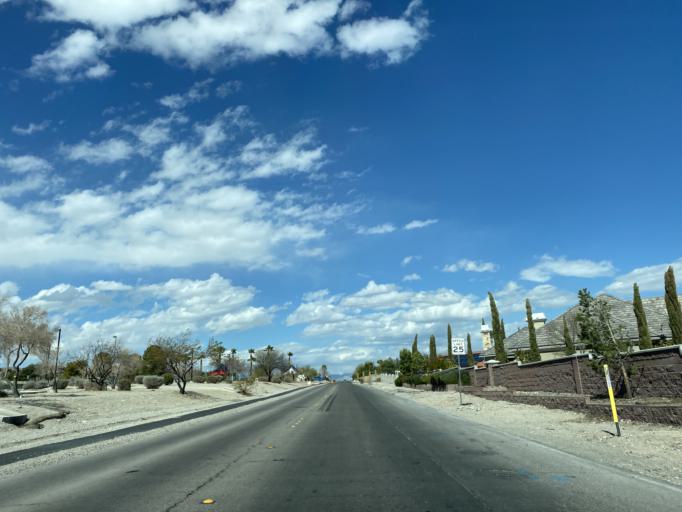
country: US
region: Nevada
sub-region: Clark County
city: Summerlin South
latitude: 36.2407
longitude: -115.3085
